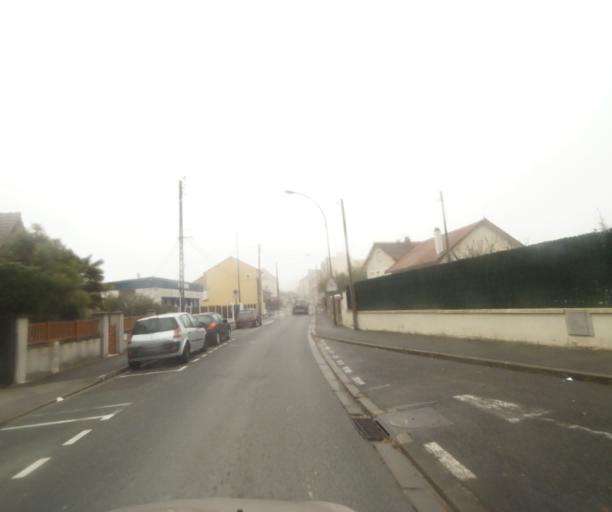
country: FR
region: Ile-de-France
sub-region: Departement de Seine-Saint-Denis
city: Vaujours
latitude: 48.9366
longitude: 2.5685
